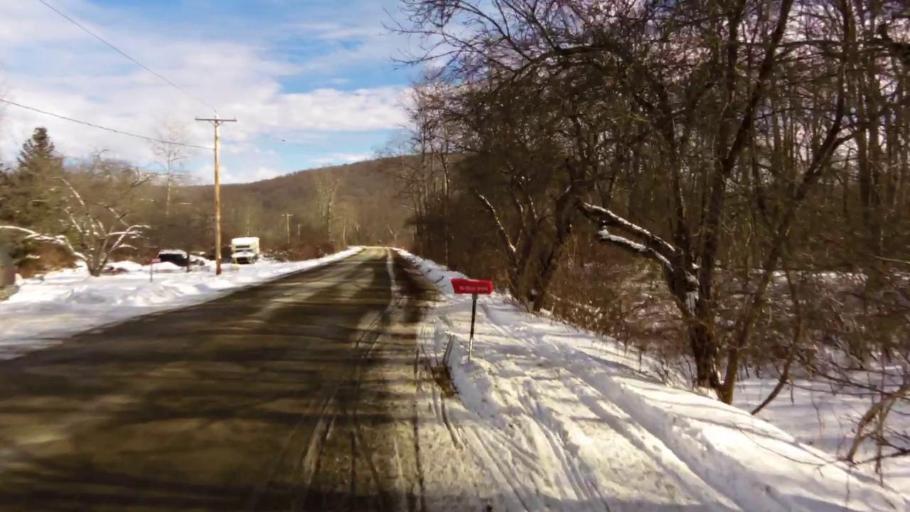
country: US
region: Pennsylvania
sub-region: McKean County
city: Foster Brook
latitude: 42.0644
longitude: -78.6443
